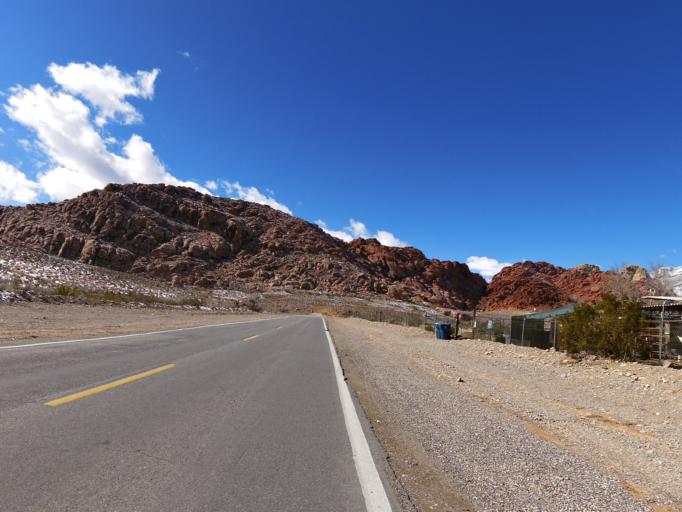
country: US
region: Nevada
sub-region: Clark County
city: Summerlin South
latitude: 36.1474
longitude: -115.4140
